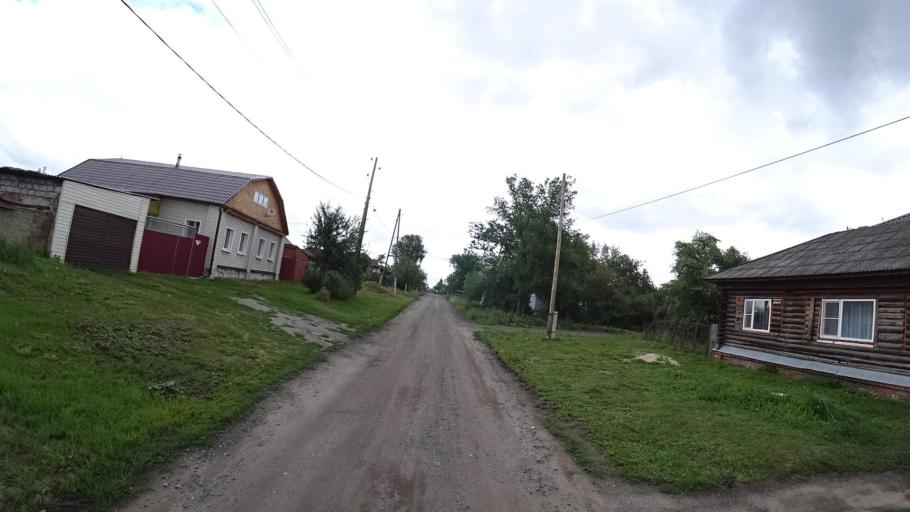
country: RU
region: Sverdlovsk
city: Kamyshlov
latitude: 56.8503
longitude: 62.6865
